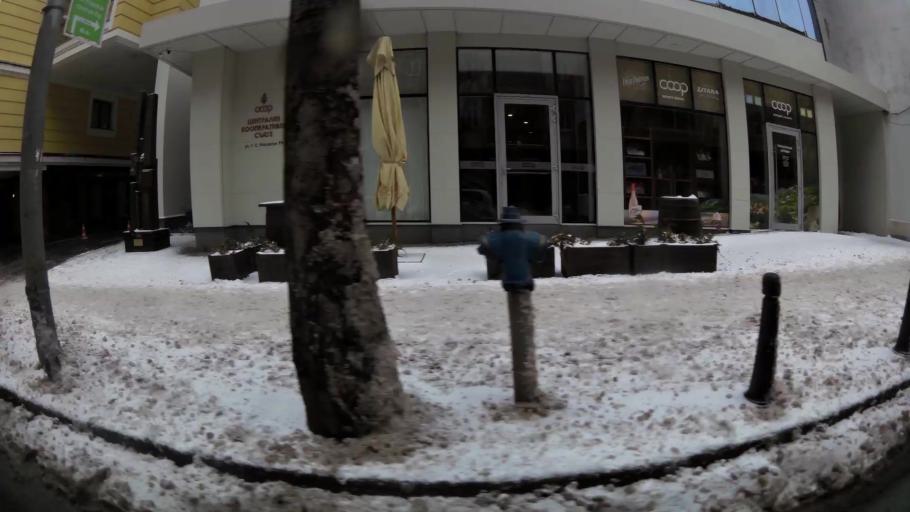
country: BG
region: Sofia-Capital
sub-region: Stolichna Obshtina
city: Sofia
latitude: 42.6994
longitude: 23.3297
